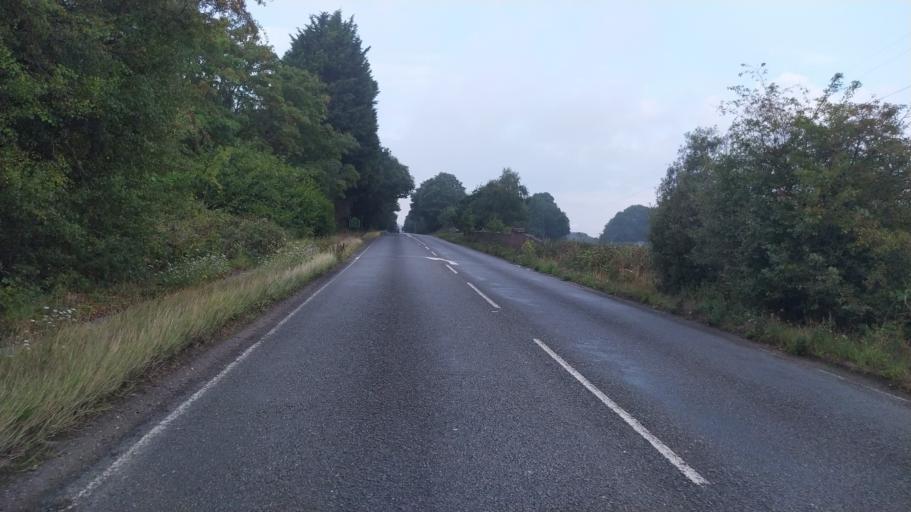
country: GB
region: England
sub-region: Hampshire
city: Bransgore
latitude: 50.7515
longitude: -1.7240
